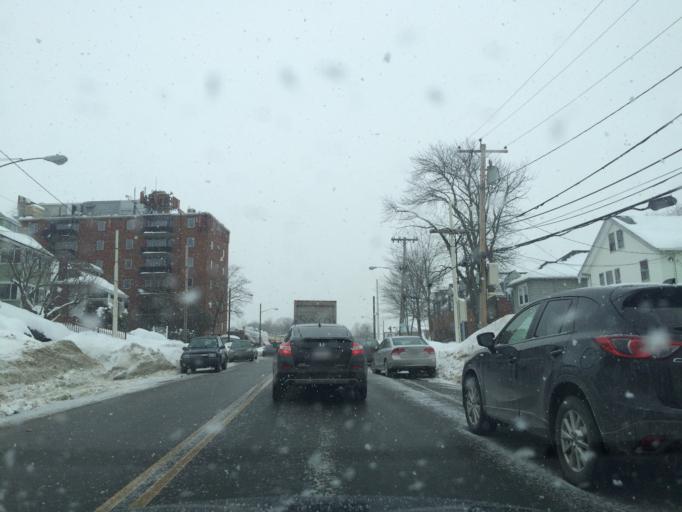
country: US
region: Massachusetts
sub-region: Middlesex County
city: Watertown
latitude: 42.3813
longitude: -71.1768
